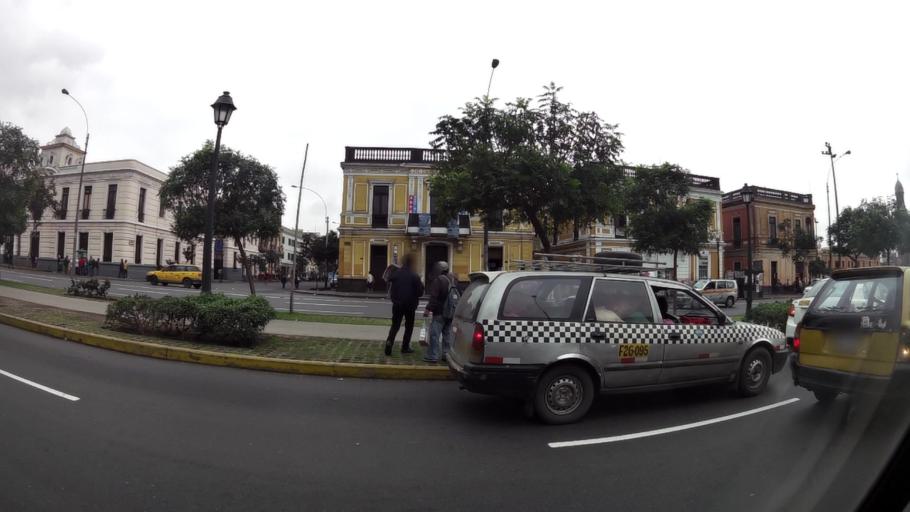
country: PE
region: Lima
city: Lima
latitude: -12.0601
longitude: -77.0406
